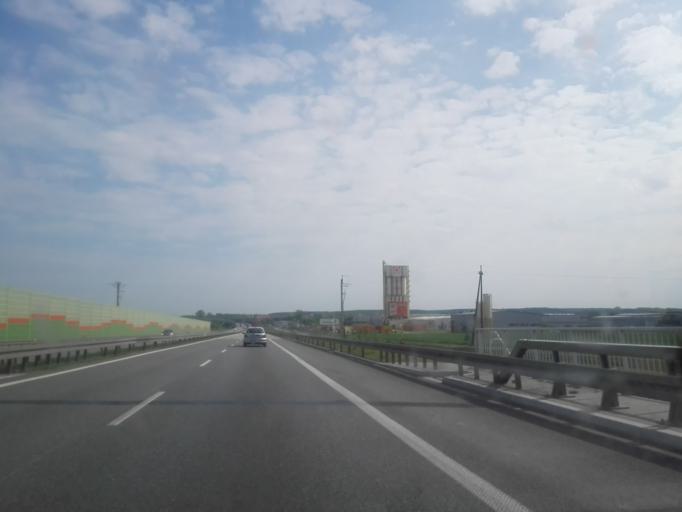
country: PL
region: Lodz Voivodeship
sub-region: Powiat rawski
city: Rawa Mazowiecka
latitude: 51.7598
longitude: 20.2625
